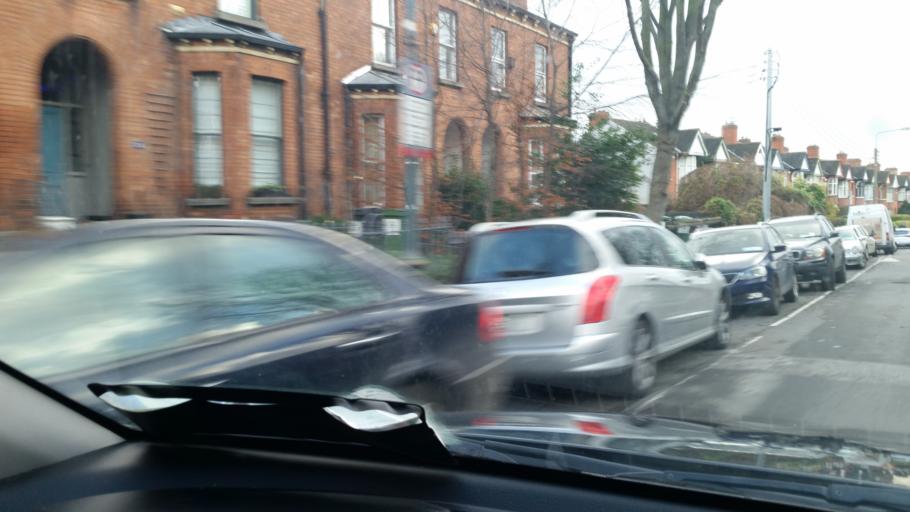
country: IE
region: Leinster
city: Cabra
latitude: 53.3574
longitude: -6.2792
